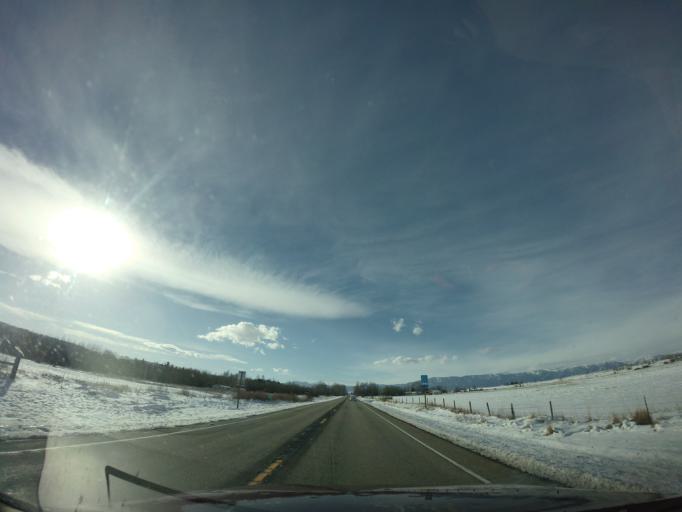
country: US
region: Montana
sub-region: Carbon County
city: Red Lodge
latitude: 45.3287
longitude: -109.1867
